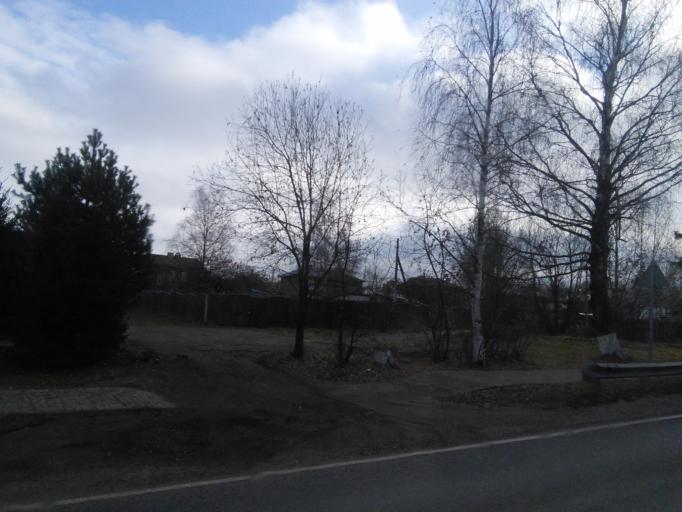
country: RU
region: Moskovskaya
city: Likino-Dulevo
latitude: 55.7103
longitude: 38.9577
